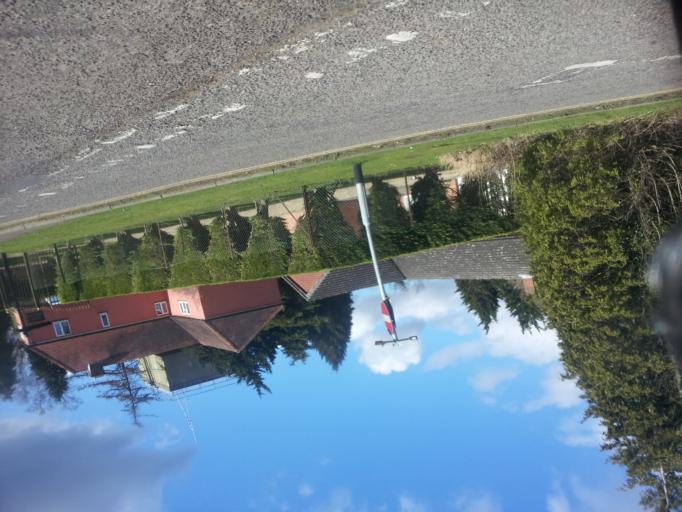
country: GB
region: England
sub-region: Kent
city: Aylesford
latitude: 51.3319
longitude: 0.5012
